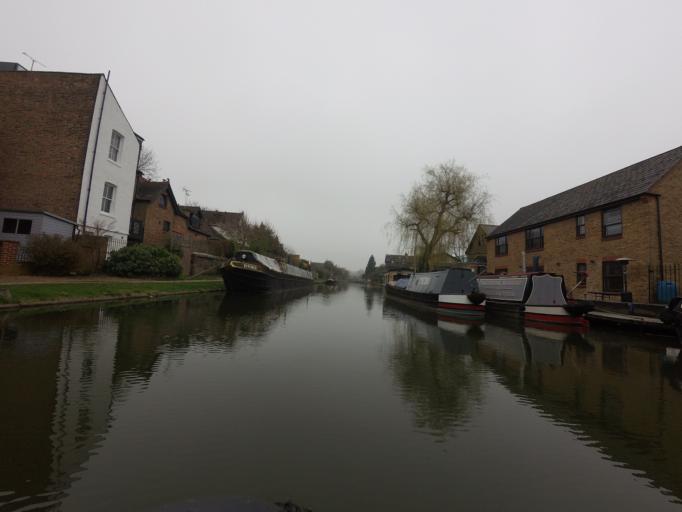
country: GB
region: England
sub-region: Hertfordshire
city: Berkhamsted
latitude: 51.7617
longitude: -0.5587
